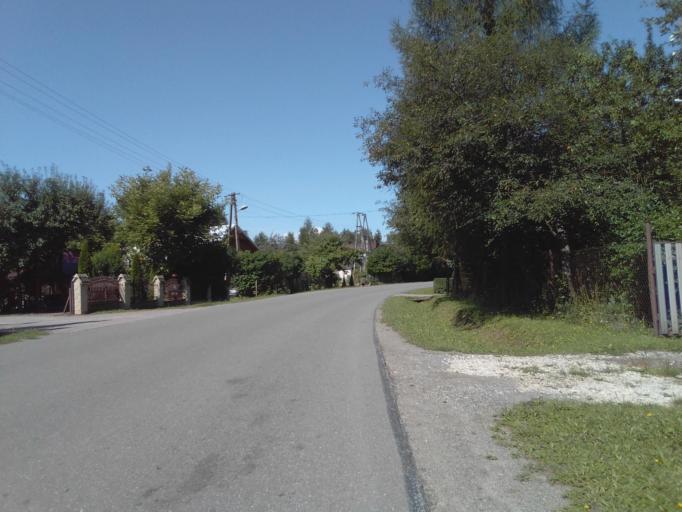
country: PL
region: Subcarpathian Voivodeship
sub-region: Powiat krosnienski
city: Dukla
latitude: 49.5996
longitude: 21.6914
